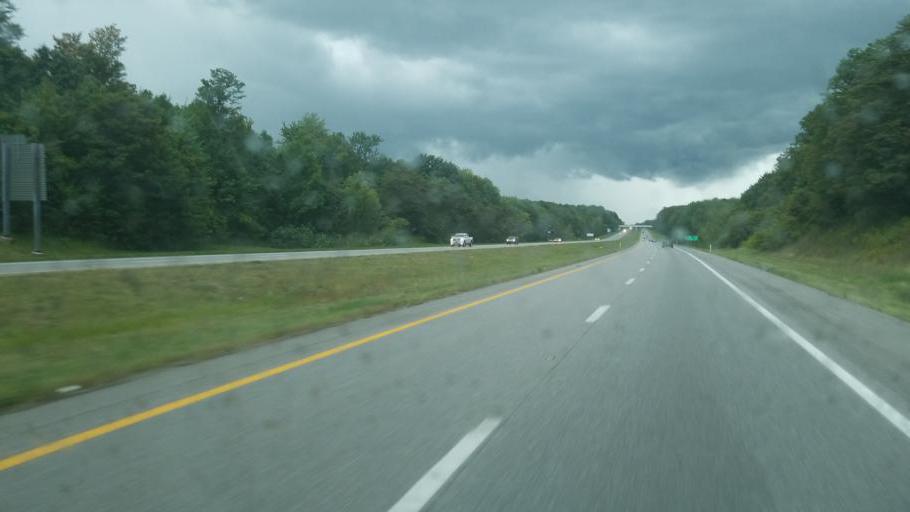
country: US
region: Ohio
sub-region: Portage County
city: Mantua
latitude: 41.3843
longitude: -81.2309
